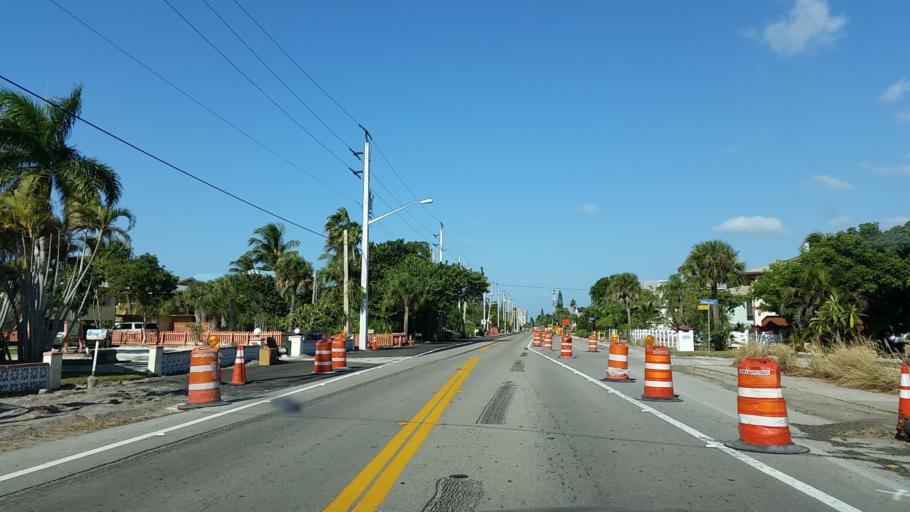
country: US
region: Florida
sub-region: Lee County
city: Fort Myers Beach
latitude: 26.4403
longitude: -81.9269
